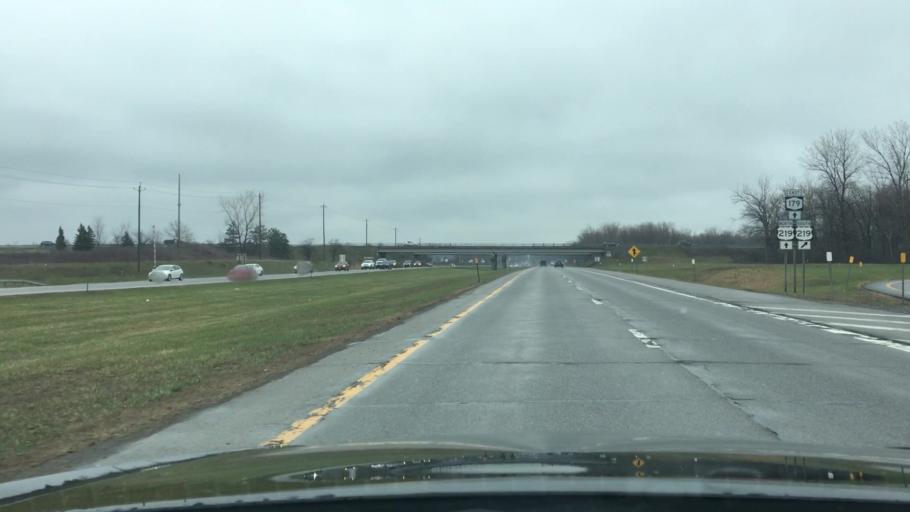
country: US
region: New York
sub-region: Erie County
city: Orchard Park
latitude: 42.7890
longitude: -78.7782
